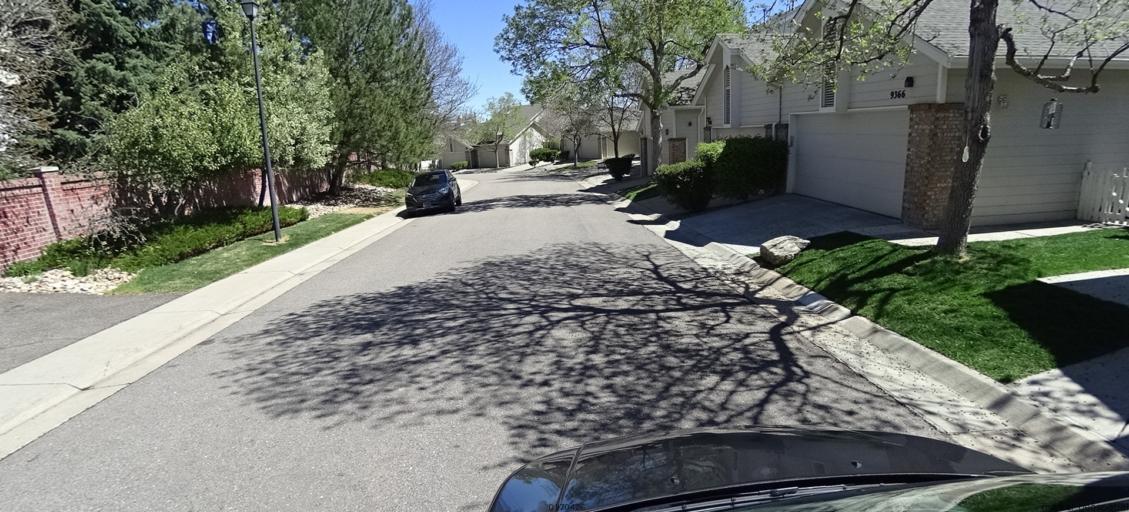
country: US
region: Colorado
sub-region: Adams County
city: Lone Tree
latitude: 39.5459
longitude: -104.8938
